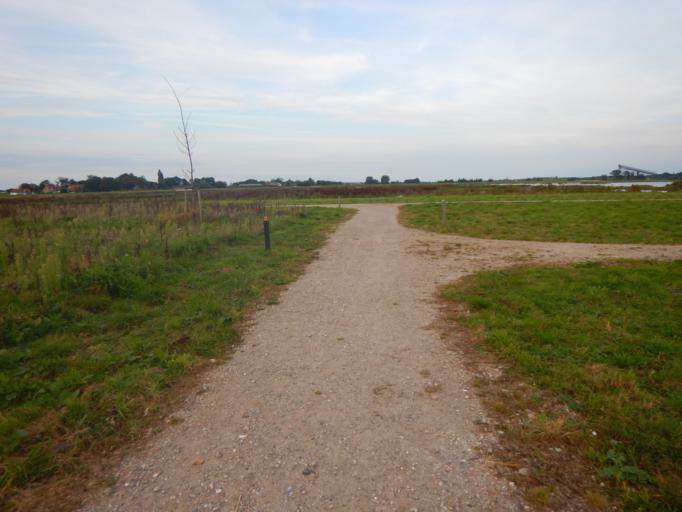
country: NL
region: South Holland
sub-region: Gemeente Pijnacker-Nootdorp
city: Pijnacker
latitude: 52.0701
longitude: 4.4219
